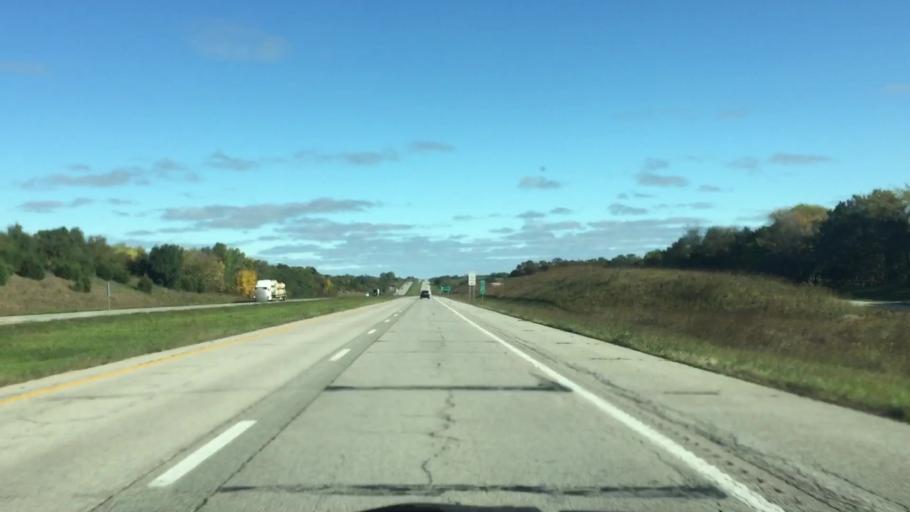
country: US
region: Missouri
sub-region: Harrison County
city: Bethany
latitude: 40.3821
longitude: -94.0006
